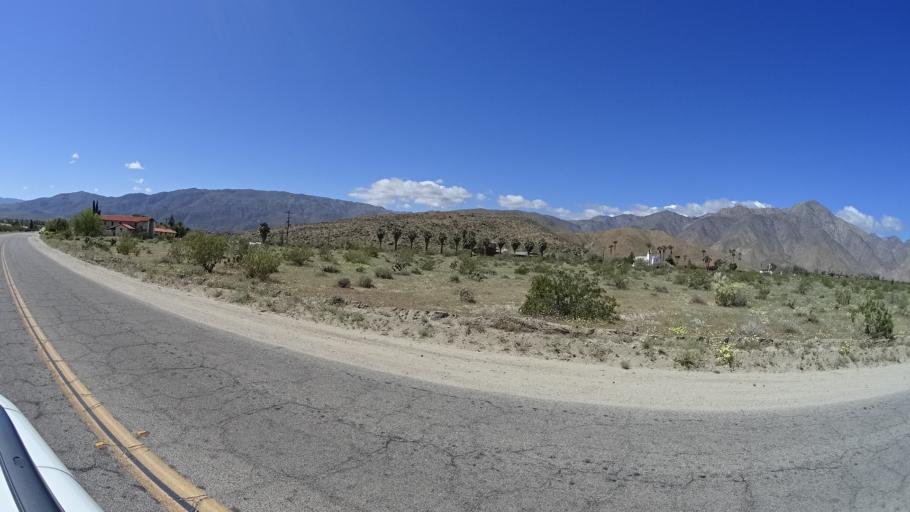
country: US
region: California
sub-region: San Diego County
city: Borrego Springs
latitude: 33.2515
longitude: -116.3768
